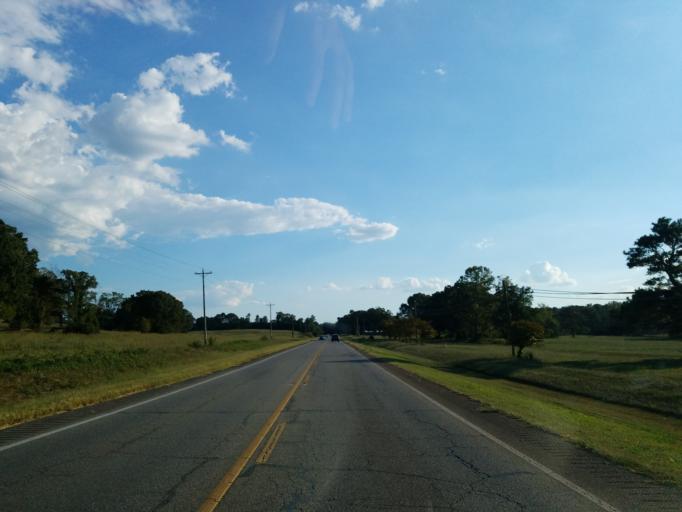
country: US
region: Georgia
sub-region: Murray County
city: Chatsworth
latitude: 34.8764
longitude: -84.7513
